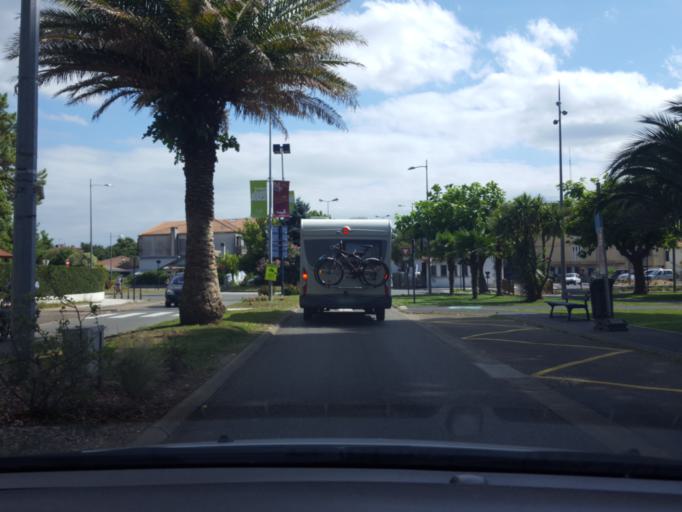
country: FR
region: Aquitaine
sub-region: Departement des Landes
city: Capbreton
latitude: 43.6416
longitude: -1.4257
